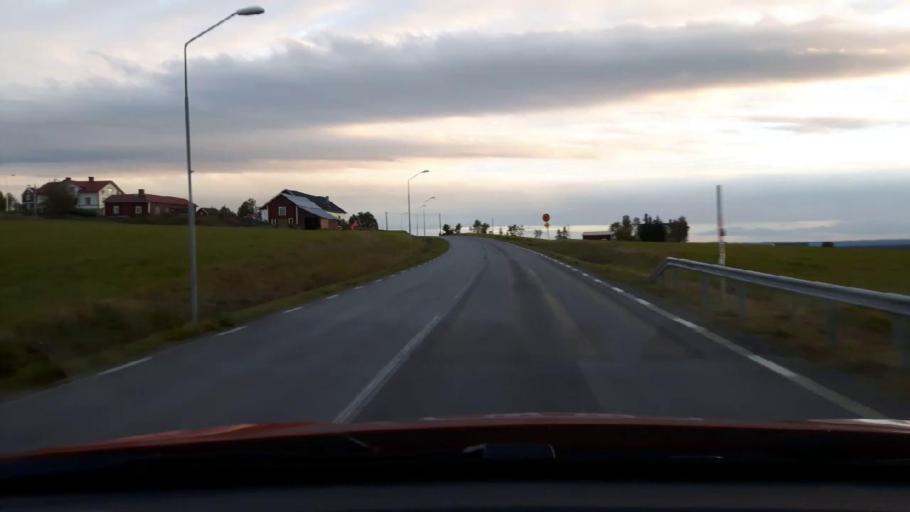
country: SE
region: Jaemtland
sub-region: OEstersunds Kommun
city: Ostersund
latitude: 63.1072
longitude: 14.4346
